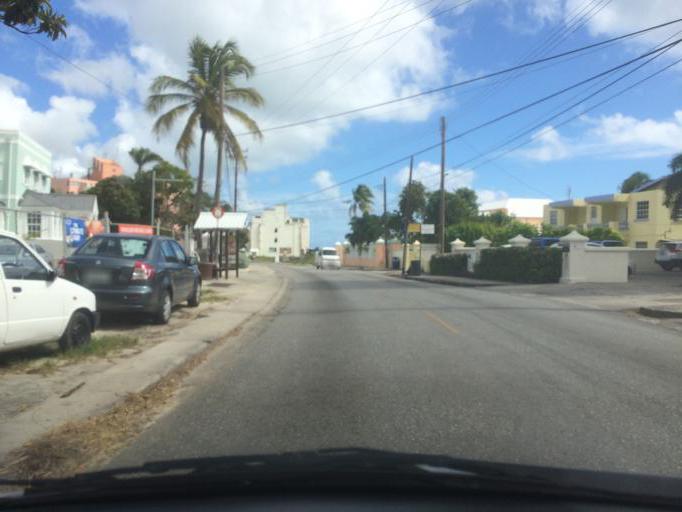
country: BB
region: Saint Michael
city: Bridgetown
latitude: 13.0747
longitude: -59.5995
